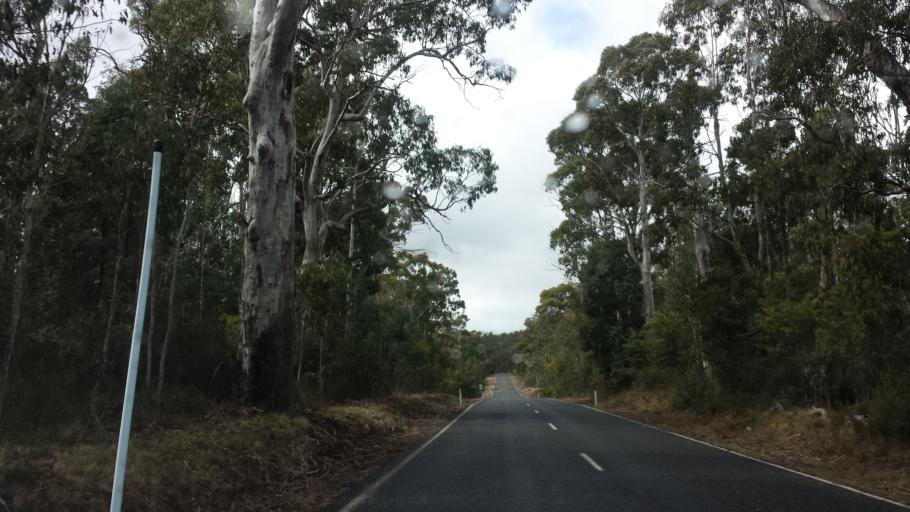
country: AU
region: Victoria
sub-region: Alpine
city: Mount Beauty
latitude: -37.1317
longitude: 147.5164
